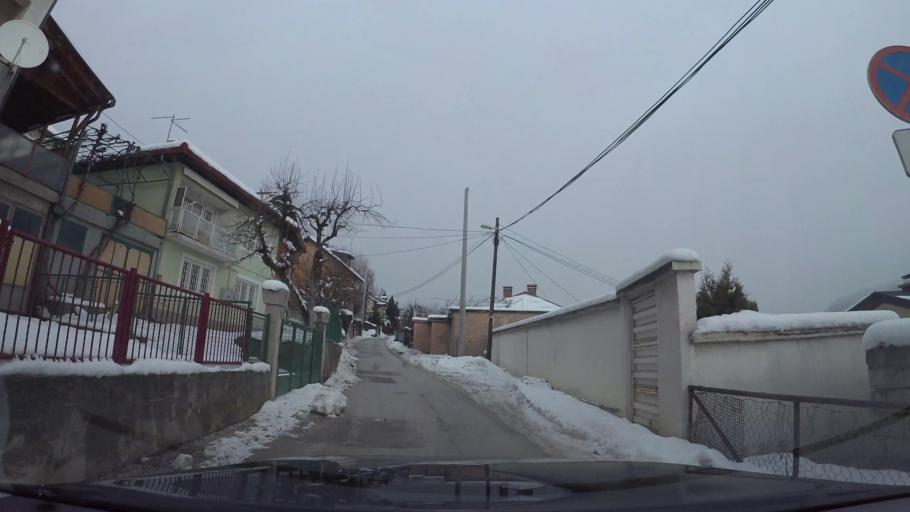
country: BA
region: Federation of Bosnia and Herzegovina
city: Kobilja Glava
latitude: 43.8668
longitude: 18.3979
